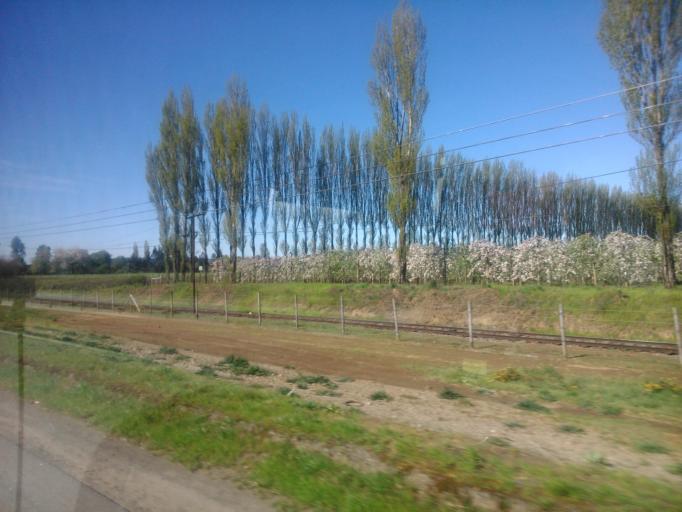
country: CL
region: Araucania
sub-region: Provincia de Cautin
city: Freire
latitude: -38.8783
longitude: -72.6180
